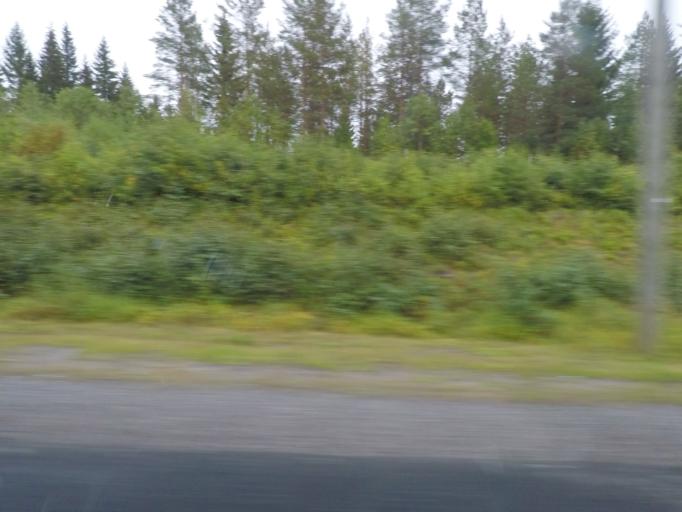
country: FI
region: Northern Savo
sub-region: Kuopio
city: Kuopio
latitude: 62.7283
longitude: 27.5846
